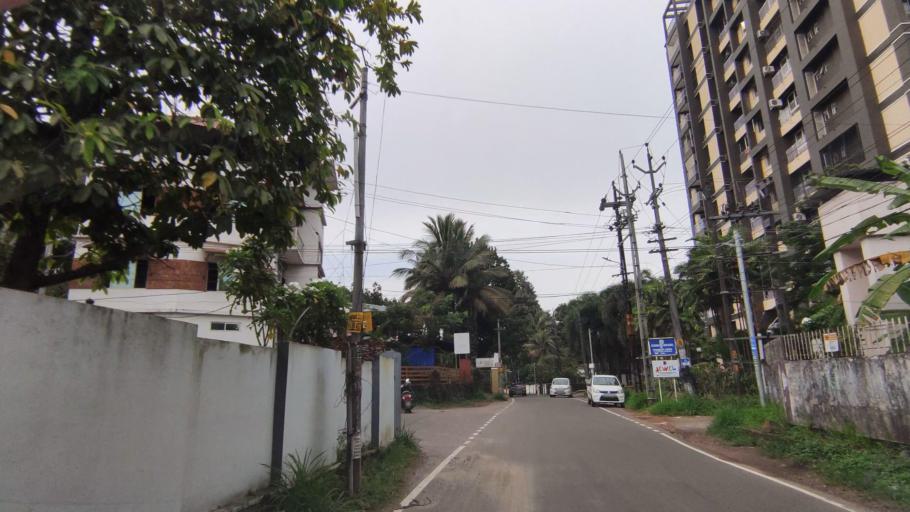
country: IN
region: Kerala
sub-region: Kottayam
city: Kottayam
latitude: 9.5938
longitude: 76.5119
